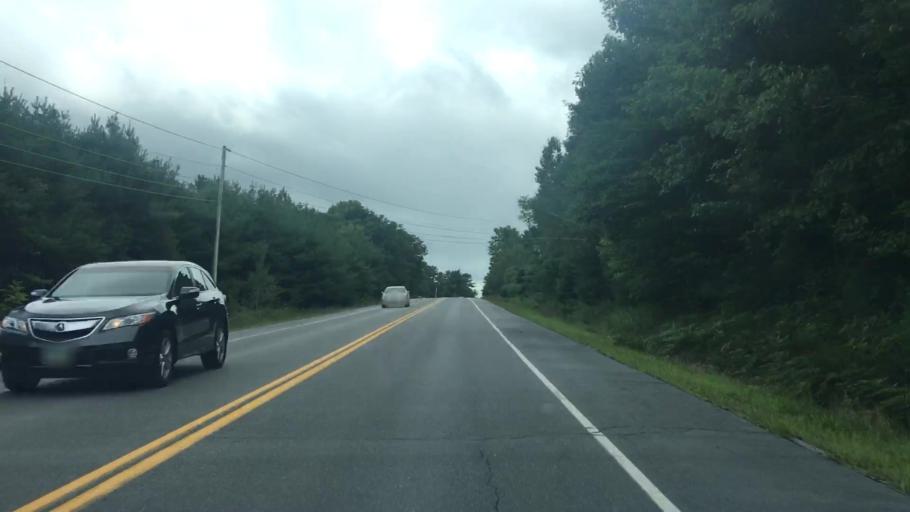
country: US
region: Maine
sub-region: York County
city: Cornish
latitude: 43.7505
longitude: -70.8125
